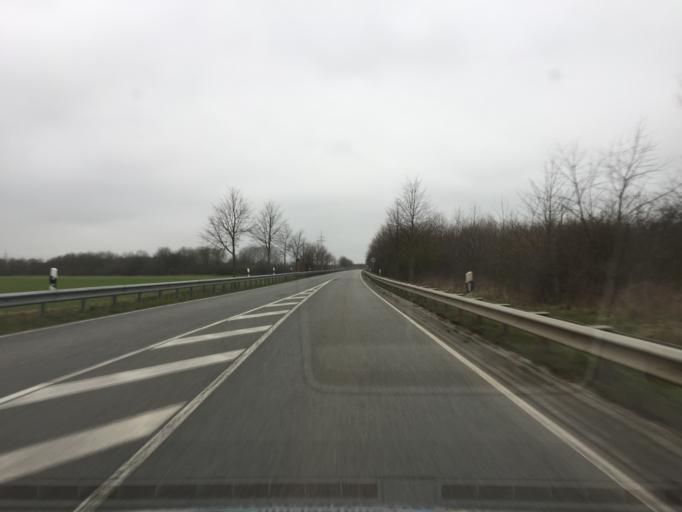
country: DE
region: North Rhine-Westphalia
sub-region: Regierungsbezirk Detmold
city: Petershagen
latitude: 52.3739
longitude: 9.0354
